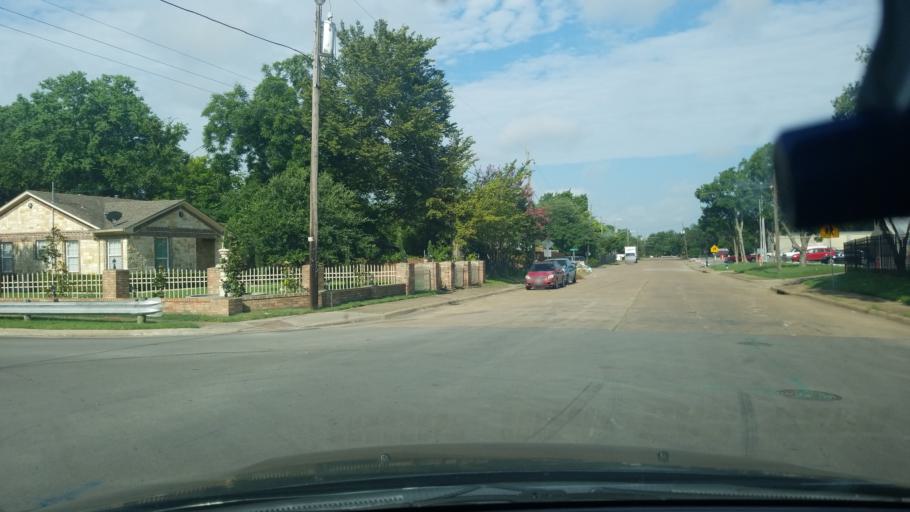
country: US
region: Texas
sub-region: Dallas County
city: Balch Springs
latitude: 32.7429
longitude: -96.6742
